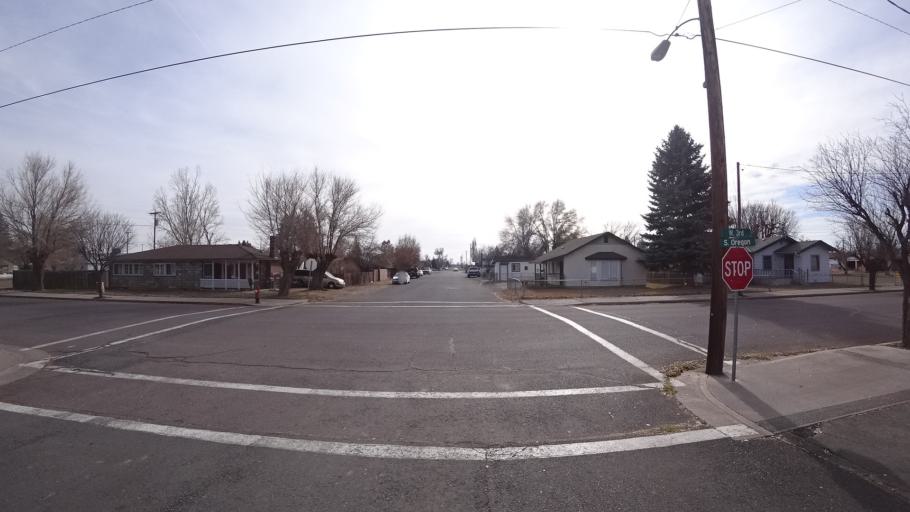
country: US
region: Oregon
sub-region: Klamath County
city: Klamath Falls
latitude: 41.9643
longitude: -121.9207
